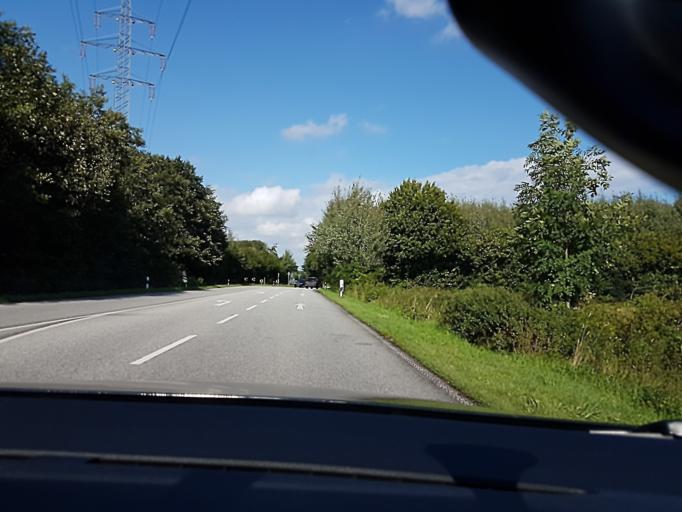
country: DE
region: Schleswig-Holstein
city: Scharbeutz
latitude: 54.0528
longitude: 10.7393
